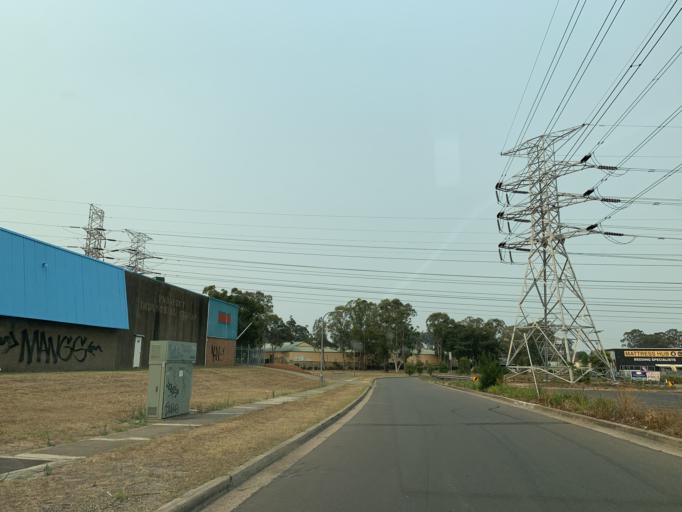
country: AU
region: New South Wales
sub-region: Holroyd
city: Girraween
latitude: -33.8008
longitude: 150.9246
